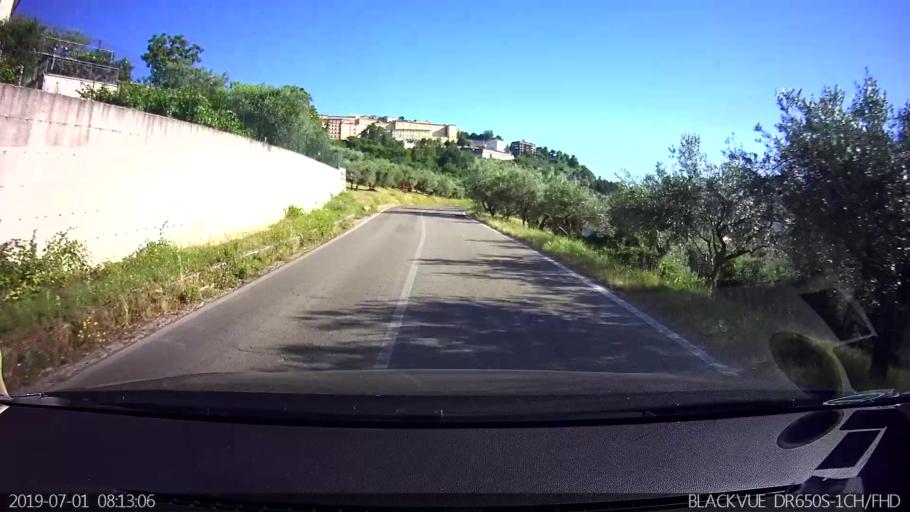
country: IT
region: Latium
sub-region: Provincia di Frosinone
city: Veroli
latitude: 41.6879
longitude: 13.4226
